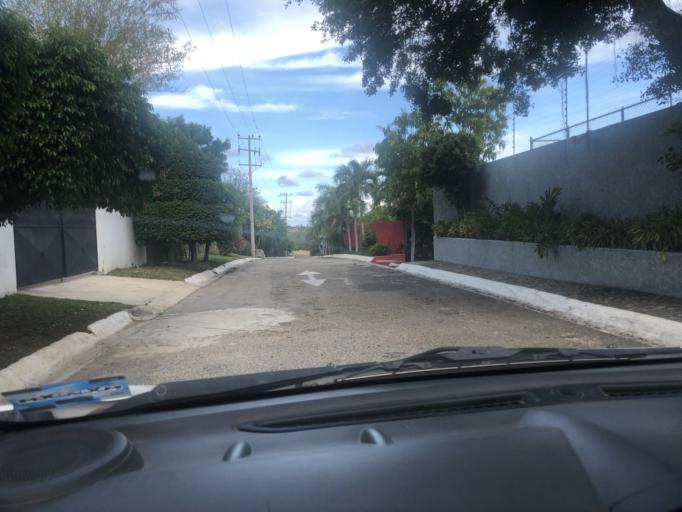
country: MX
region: Oaxaca
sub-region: Santa Maria Huatulco
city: Crucecita
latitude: 15.7717
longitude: -96.0880
